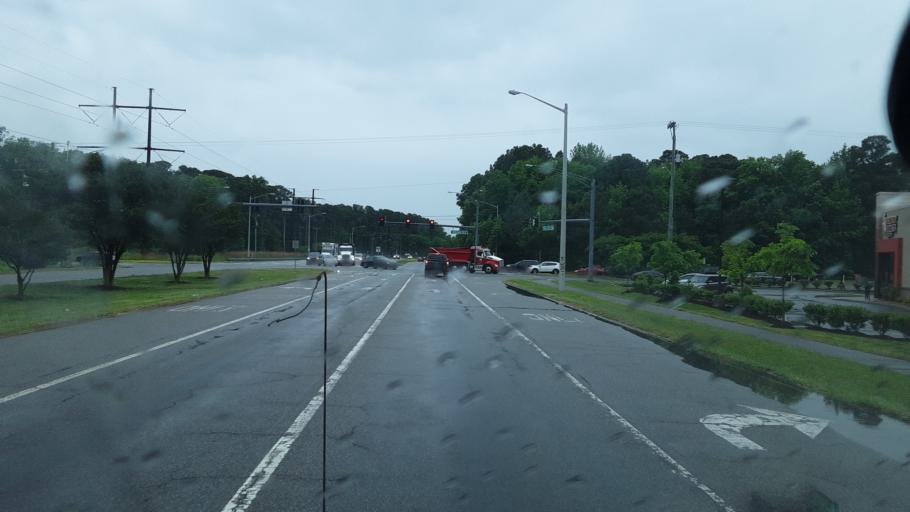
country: US
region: Virginia
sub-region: City of Virginia Beach
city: Virginia Beach
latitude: 36.7947
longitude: -75.9952
